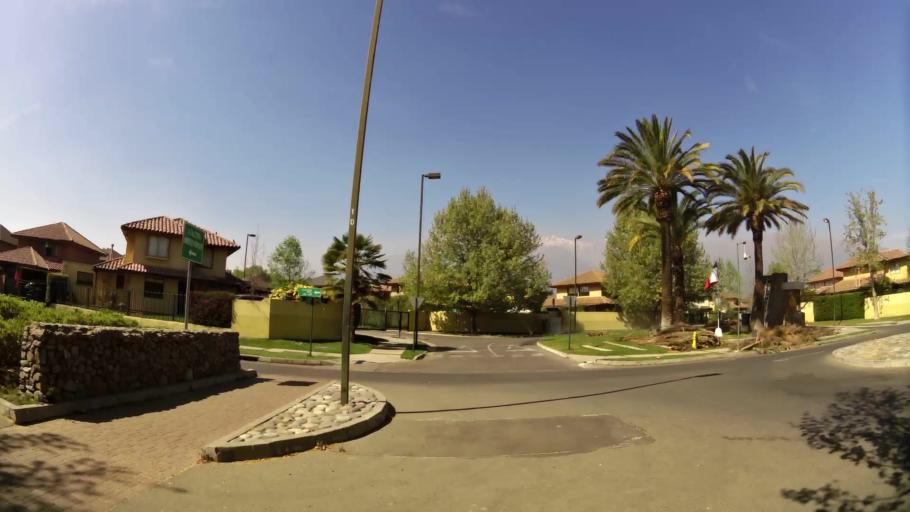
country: CL
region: Santiago Metropolitan
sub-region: Provincia de Santiago
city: Villa Presidente Frei, Nunoa, Santiago, Chile
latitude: -33.4882
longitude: -70.5751
